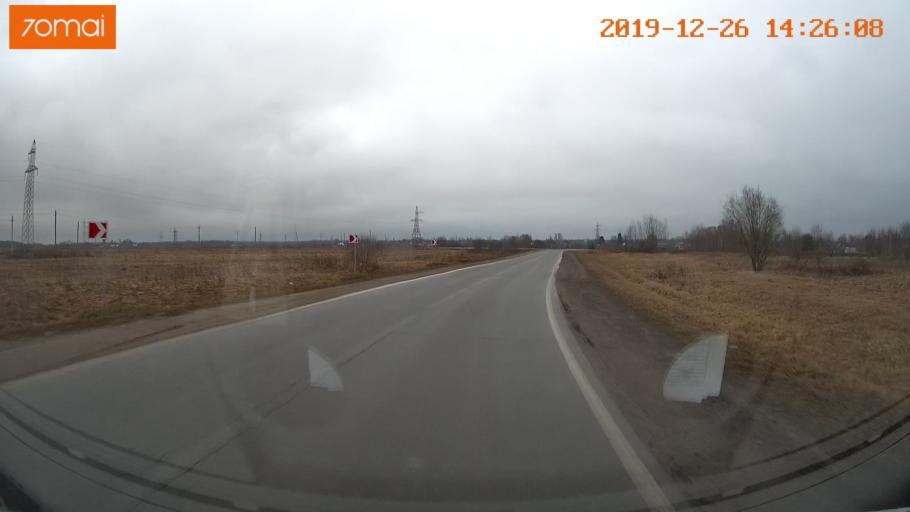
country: RU
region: Jaroslavl
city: Poshekhon'ye
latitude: 58.4885
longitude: 39.0915
